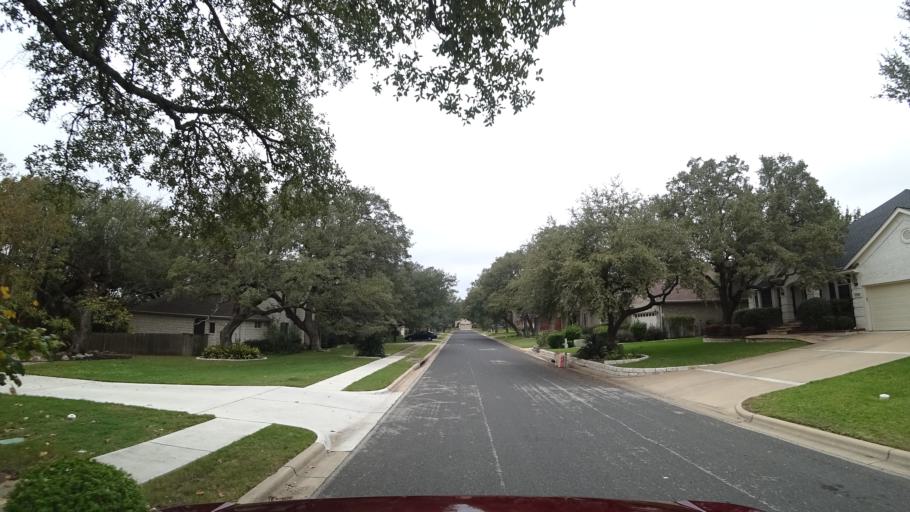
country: US
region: Texas
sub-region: Williamson County
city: Anderson Mill
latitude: 30.4482
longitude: -97.8203
